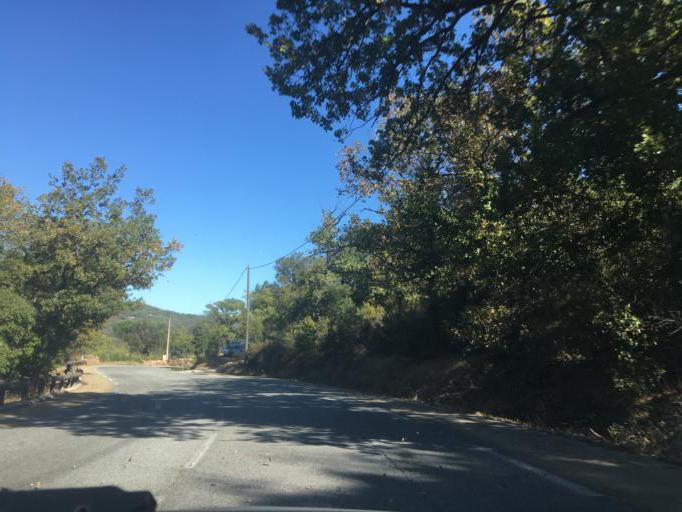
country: FR
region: Provence-Alpes-Cote d'Azur
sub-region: Departement du Var
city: La Garde-Freinet
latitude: 43.3004
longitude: 6.4805
